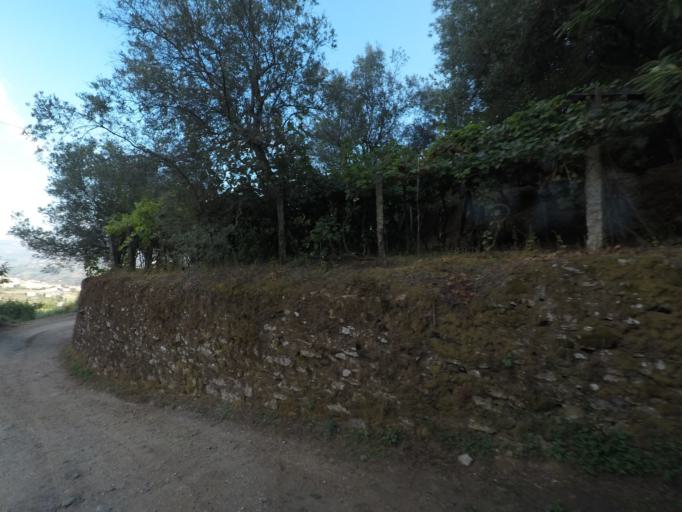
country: PT
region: Vila Real
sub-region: Mesao Frio
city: Mesao Frio
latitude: 41.1667
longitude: -7.9039
